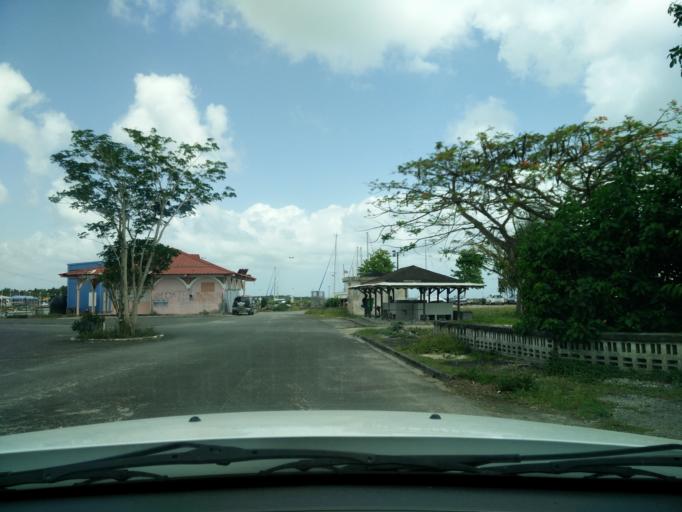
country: GP
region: Guadeloupe
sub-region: Guadeloupe
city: Port-Louis
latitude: 16.4129
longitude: -61.5322
